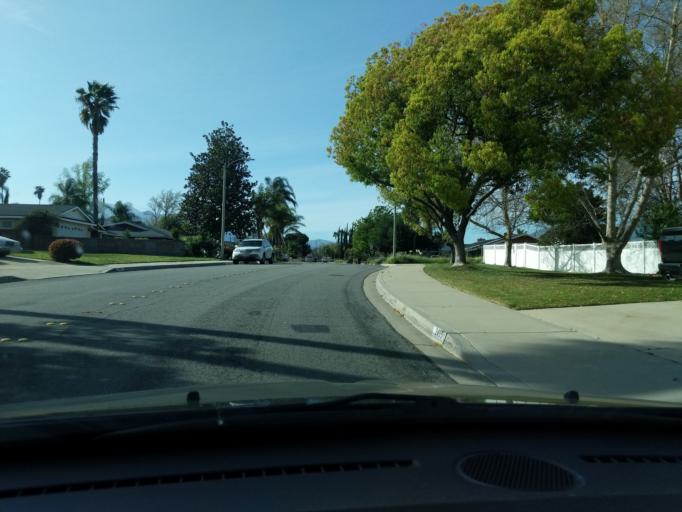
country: US
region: California
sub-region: San Bernardino County
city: Muscoy
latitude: 34.1438
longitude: -117.3725
